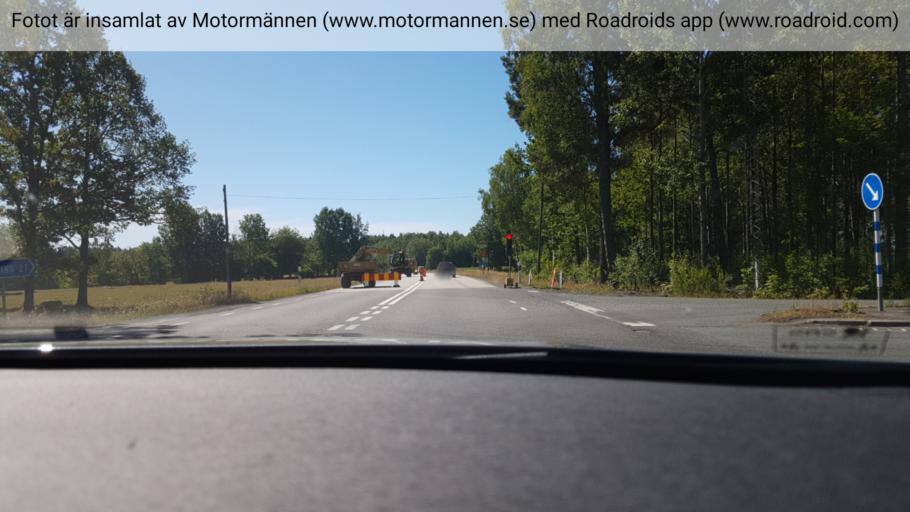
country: SE
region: Joenkoeping
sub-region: Habo Kommun
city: Habo
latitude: 57.9237
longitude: 14.0952
